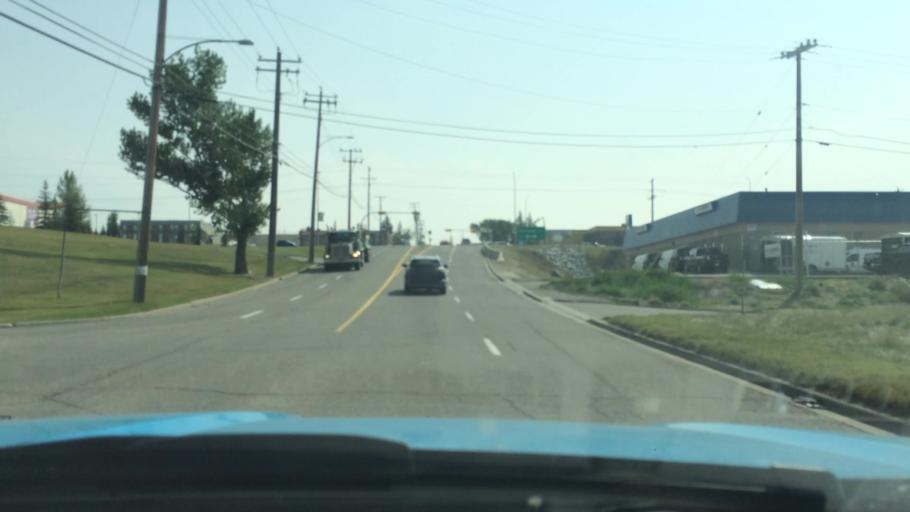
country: CA
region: Alberta
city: Calgary
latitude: 51.0525
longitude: -114.0043
